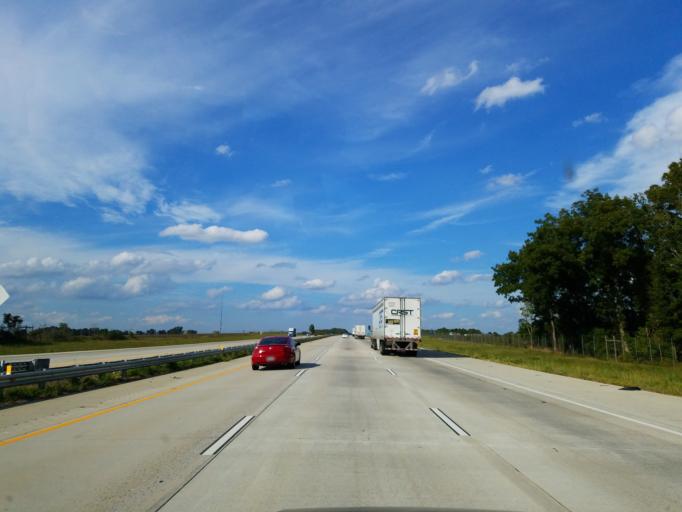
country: US
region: Georgia
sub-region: Dooly County
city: Vienna
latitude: 32.1662
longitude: -83.7534
